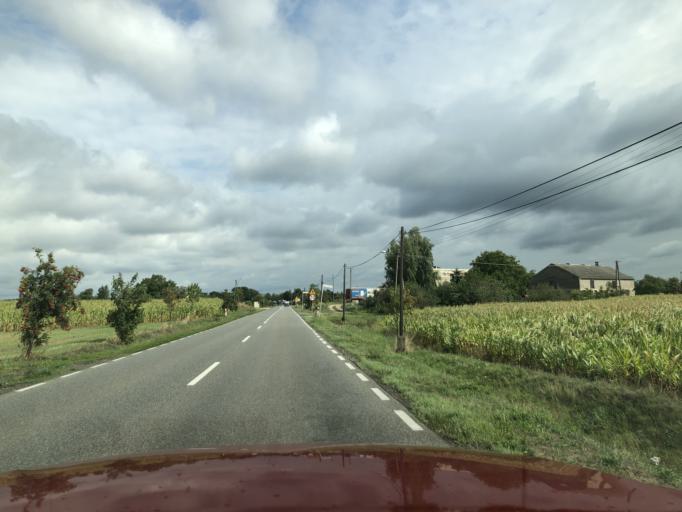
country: PL
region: Greater Poland Voivodeship
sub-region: Powiat szamotulski
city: Pniewy
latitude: 52.5325
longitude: 16.2768
